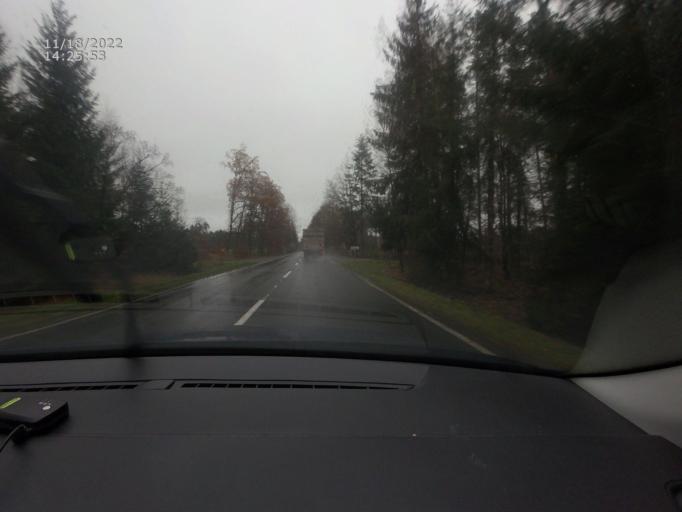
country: CZ
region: Jihocesky
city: Cimelice
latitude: 49.4329
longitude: 14.1621
